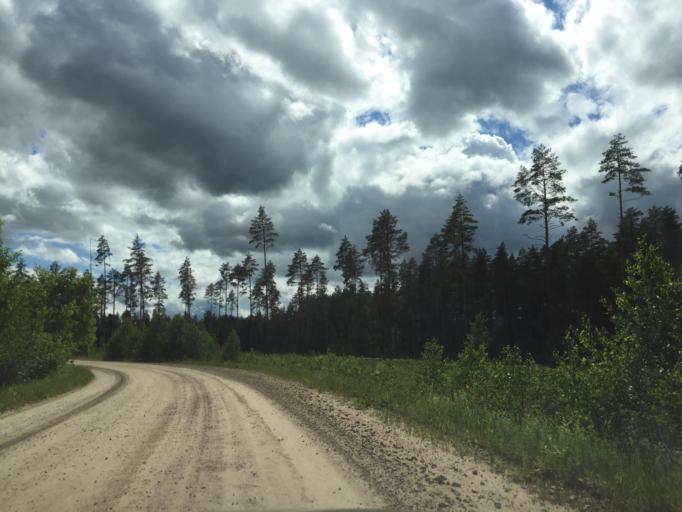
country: LV
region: Vecumnieki
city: Vecumnieki
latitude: 56.4903
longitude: 24.4079
